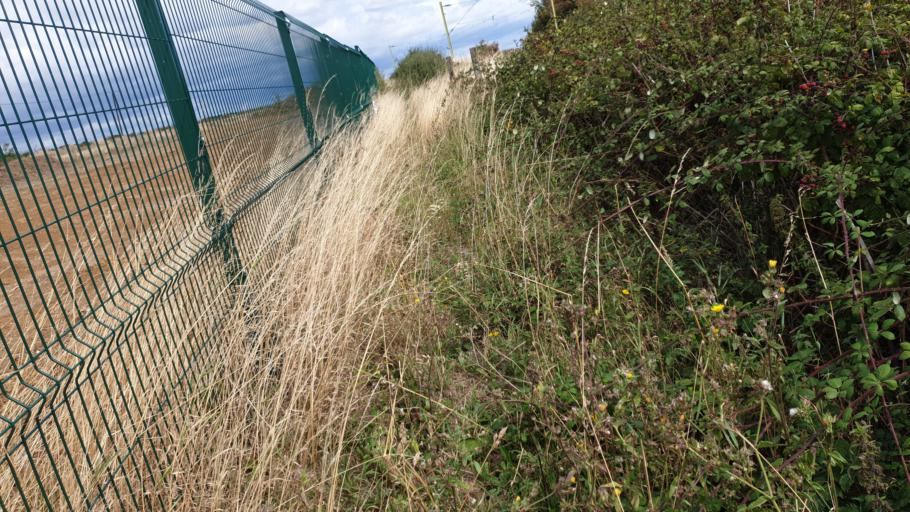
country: GB
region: England
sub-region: Essex
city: Clacton-on-Sea
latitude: 51.8178
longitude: 1.1804
